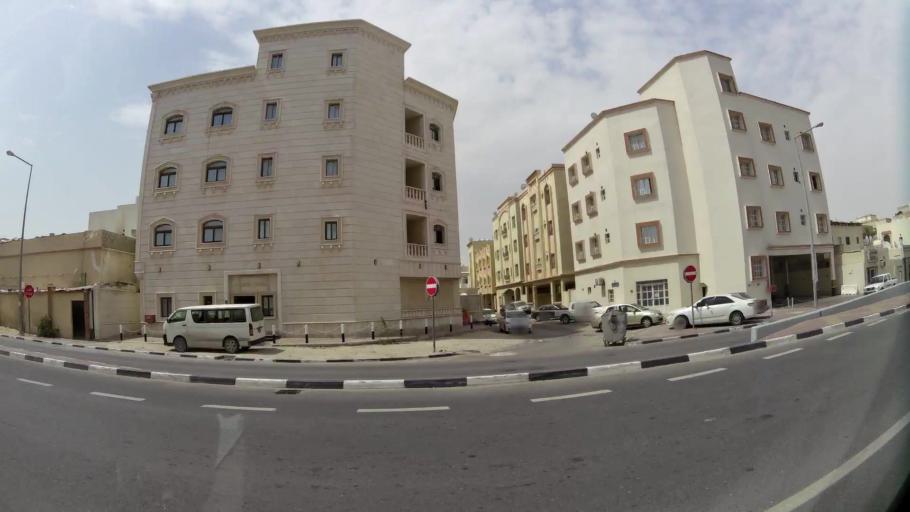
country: QA
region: Baladiyat ar Rayyan
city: Ar Rayyan
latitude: 25.3195
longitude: 51.4771
